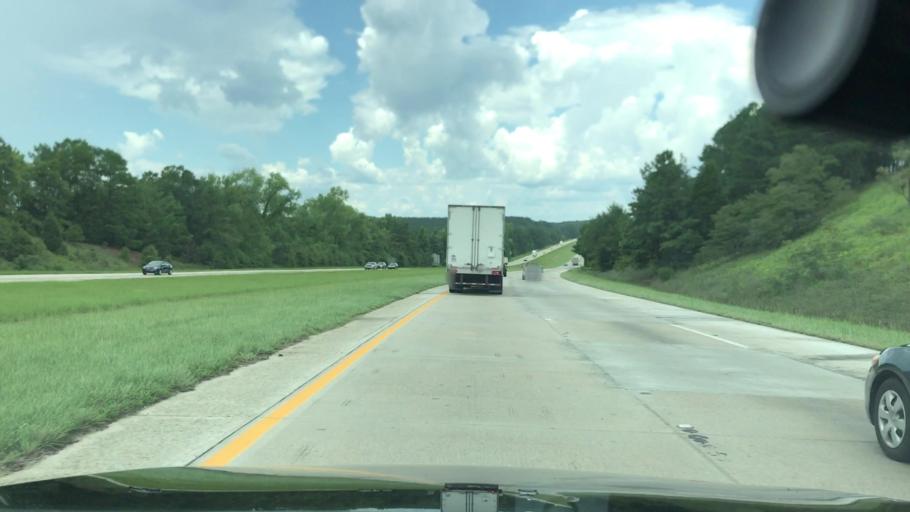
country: US
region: South Carolina
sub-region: Fairfield County
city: Winnsboro Mills
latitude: 34.3234
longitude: -81.0059
